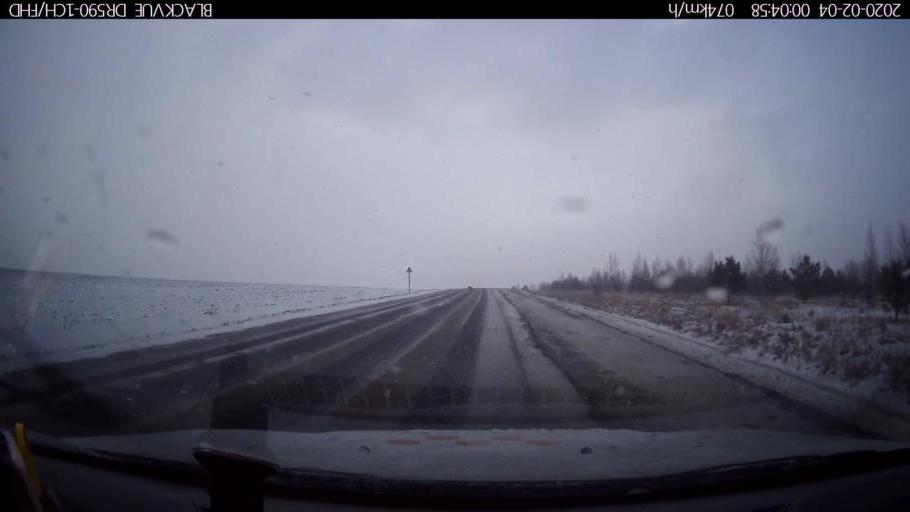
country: RU
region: Nizjnij Novgorod
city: Dal'neye Konstantinovo
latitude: 55.8316
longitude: 44.1226
